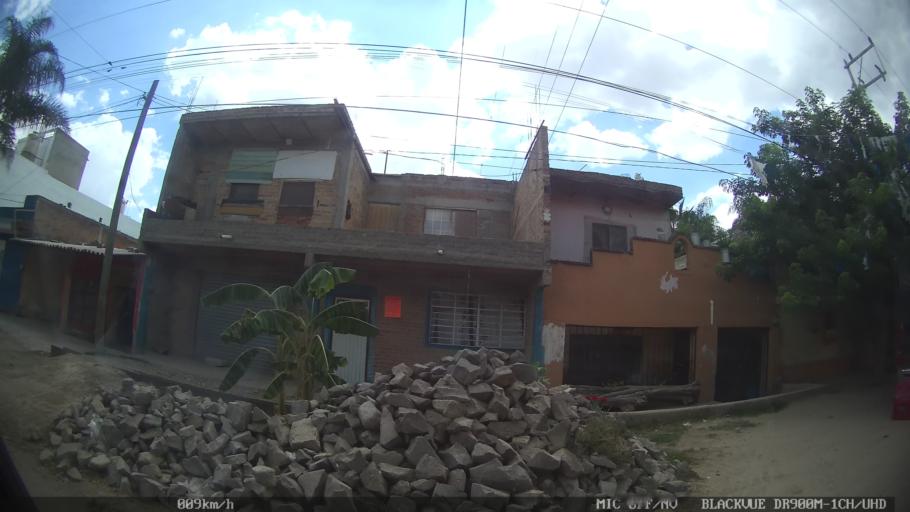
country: MX
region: Jalisco
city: Tlaquepaque
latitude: 20.6730
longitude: -103.2620
